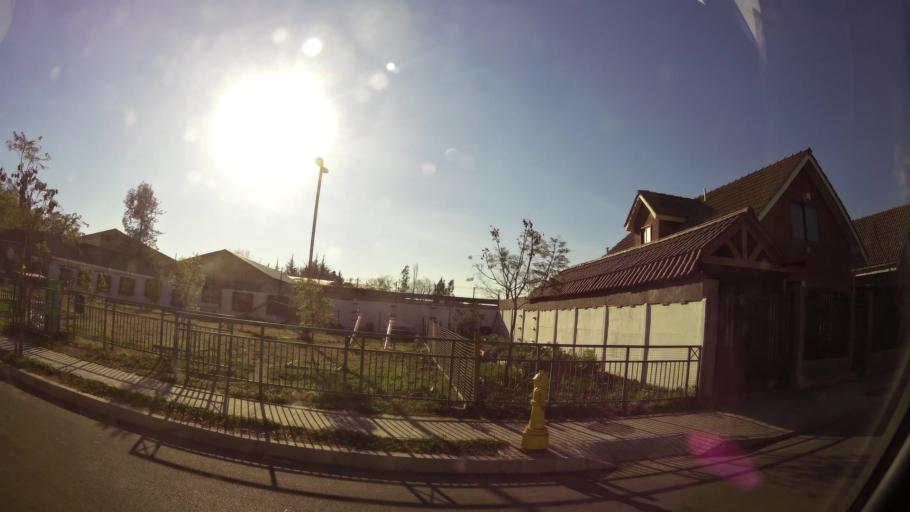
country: CL
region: Santiago Metropolitan
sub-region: Provincia de Talagante
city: Penaflor
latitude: -33.6014
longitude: -70.8574
